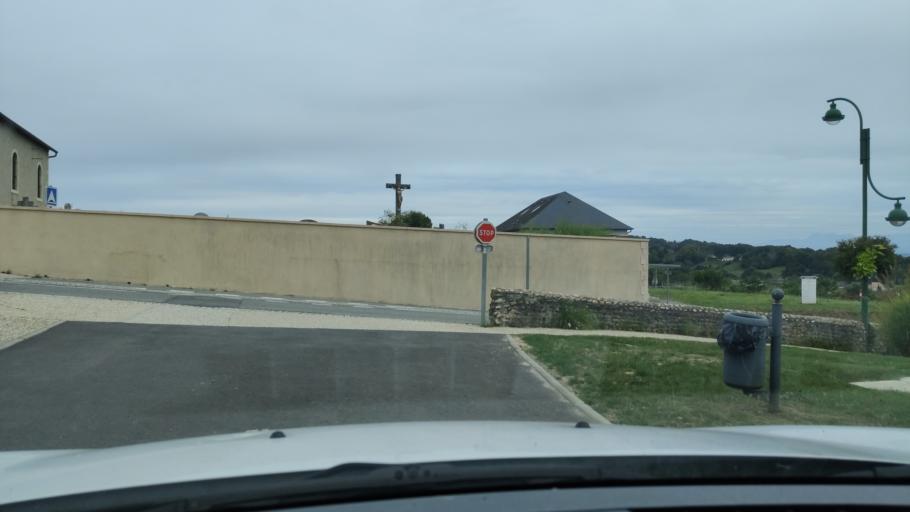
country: FR
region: Aquitaine
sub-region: Departement des Pyrenees-Atlantiques
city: Sauvagnon
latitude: 43.4030
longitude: -0.3872
